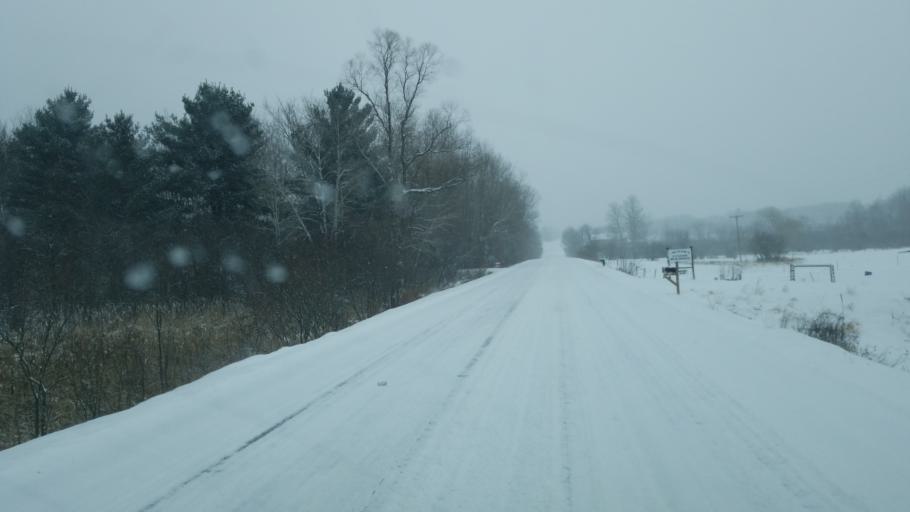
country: US
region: Michigan
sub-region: Mecosta County
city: Canadian Lakes
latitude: 43.5768
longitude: -85.4316
